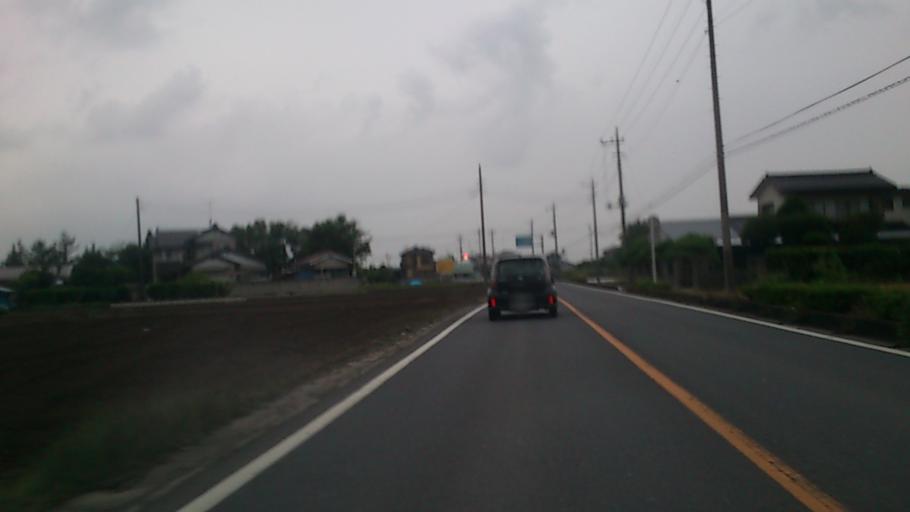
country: JP
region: Saitama
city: Kazo
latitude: 36.1621
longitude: 139.6002
